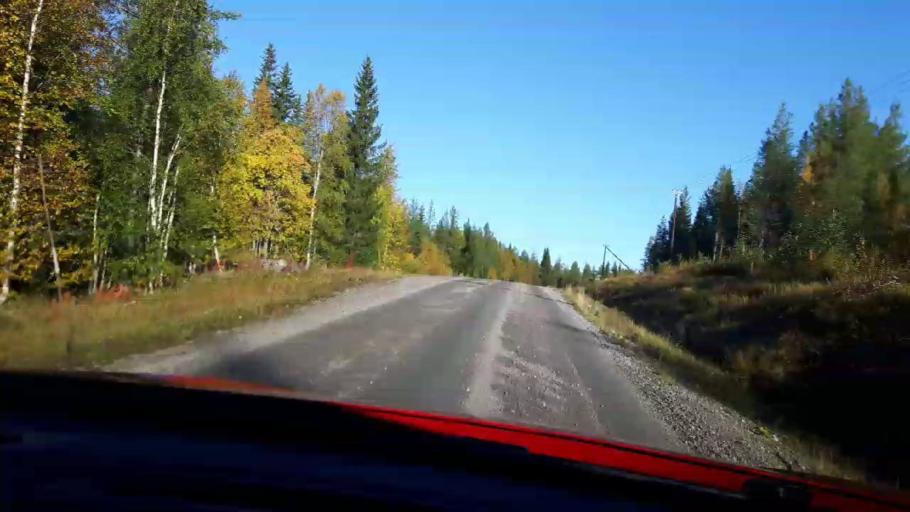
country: SE
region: Jaemtland
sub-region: Stroemsunds Kommun
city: Stroemsund
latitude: 64.3728
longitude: 15.1542
